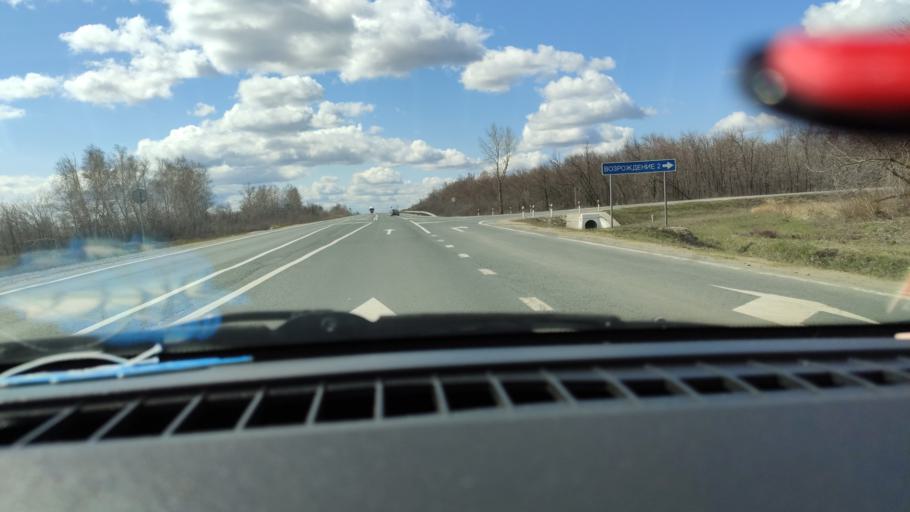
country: RU
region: Saratov
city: Dukhovnitskoye
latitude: 52.6775
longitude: 48.2290
